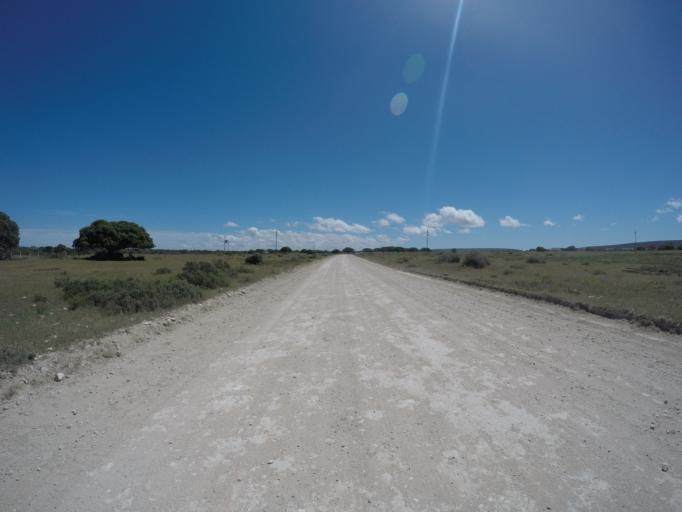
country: ZA
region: Western Cape
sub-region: Overberg District Municipality
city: Bredasdorp
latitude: -34.4559
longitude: 20.4061
